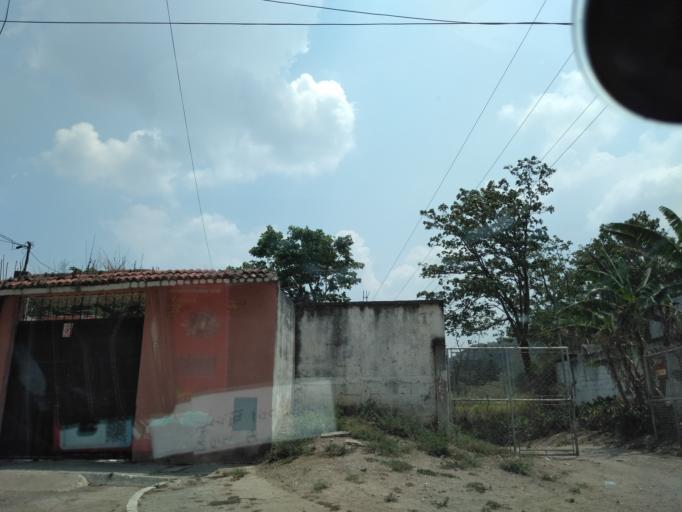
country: GT
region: Guatemala
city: Petapa
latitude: 14.5260
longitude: -90.5424
